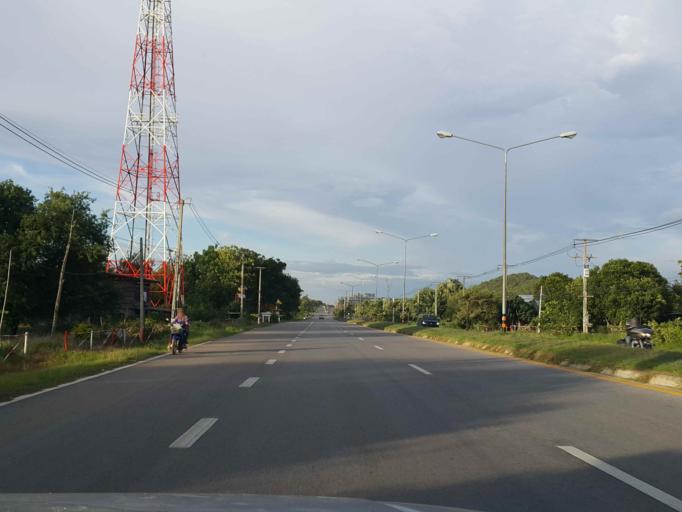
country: TH
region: Sukhothai
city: Ban Dan Lan Hoi
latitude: 16.9406
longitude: 99.4289
